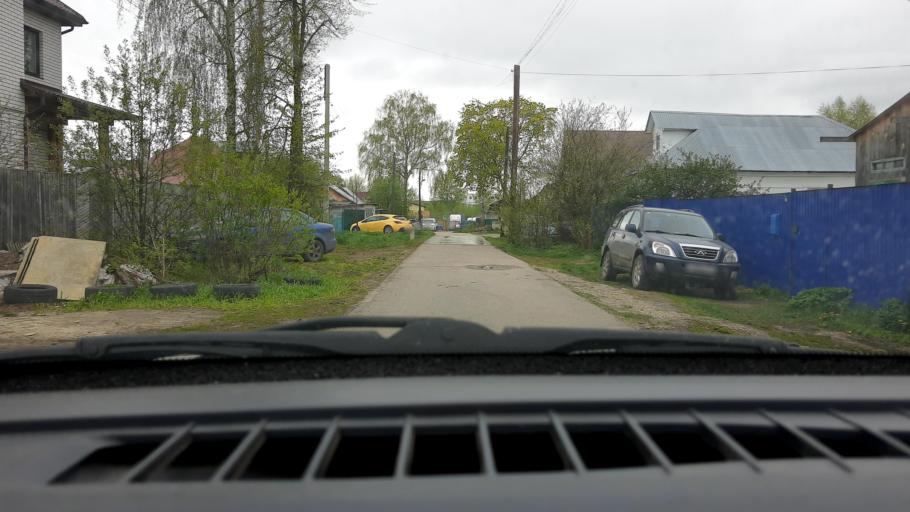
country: RU
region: Nizjnij Novgorod
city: Gorbatovka
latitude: 56.3362
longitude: 43.8241
